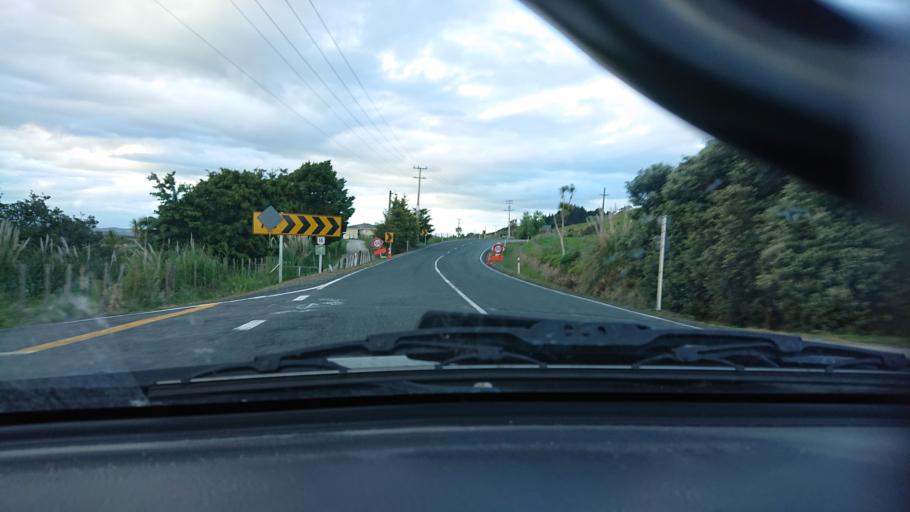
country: NZ
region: Auckland
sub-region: Auckland
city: Wellsford
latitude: -36.4502
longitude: 174.4336
